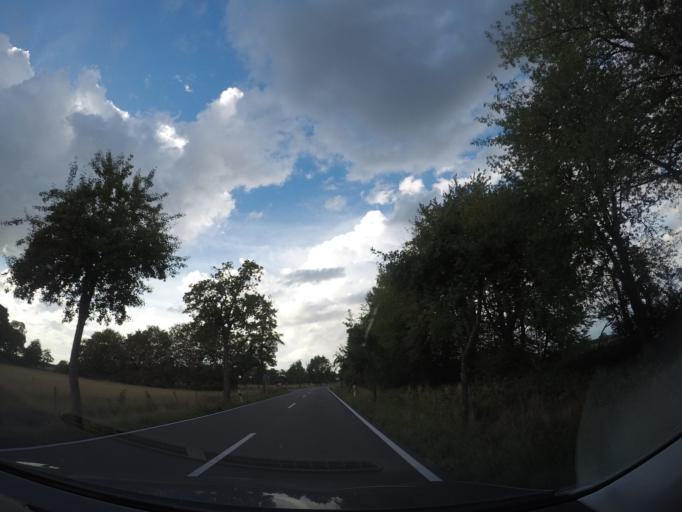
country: DE
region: Saxony-Anhalt
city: Calvorde
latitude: 52.4232
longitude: 11.3051
